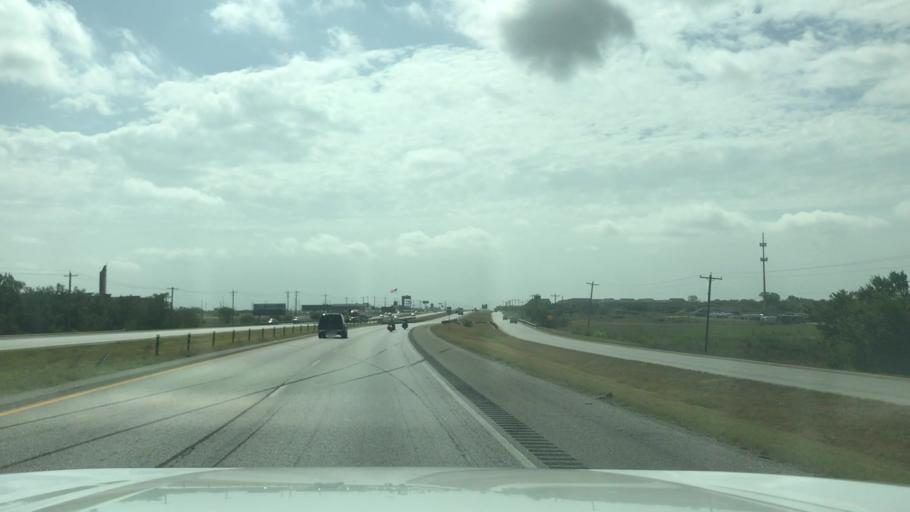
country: US
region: Texas
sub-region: Taylor County
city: Abilene
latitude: 32.4884
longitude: -99.7170
